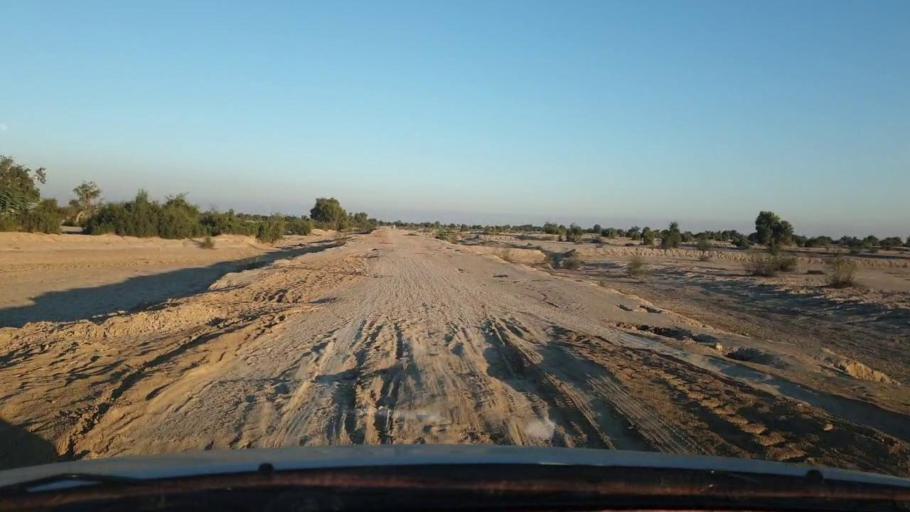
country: PK
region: Sindh
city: Johi
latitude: 26.8075
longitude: 67.4752
